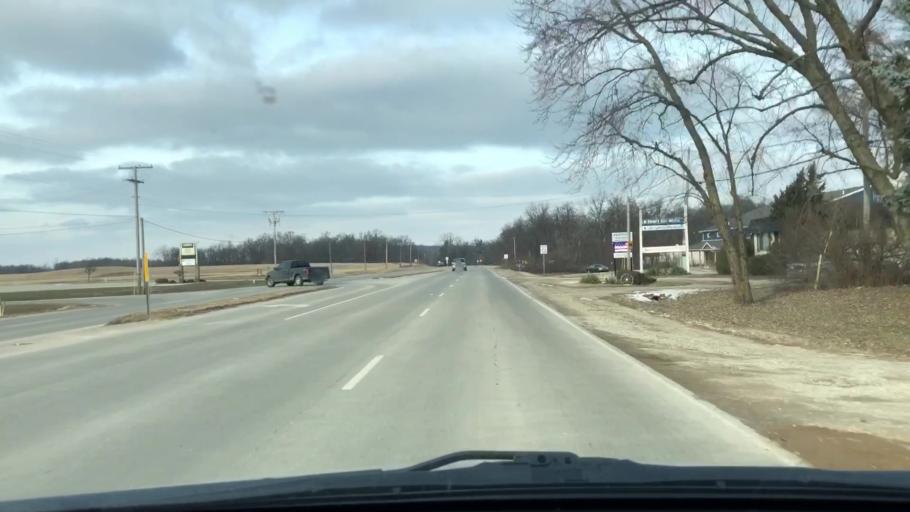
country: US
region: Indiana
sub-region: Steuben County
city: Angola
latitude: 41.6782
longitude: -85.0288
